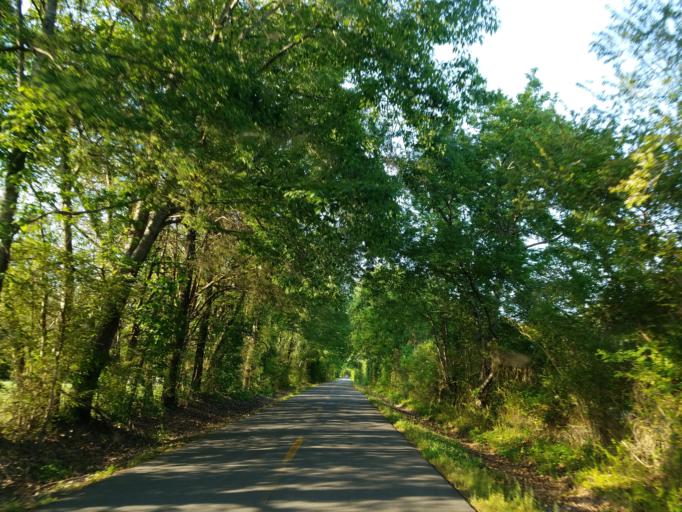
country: US
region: Georgia
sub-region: Gordon County
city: Calhoun
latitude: 34.5323
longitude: -85.1101
